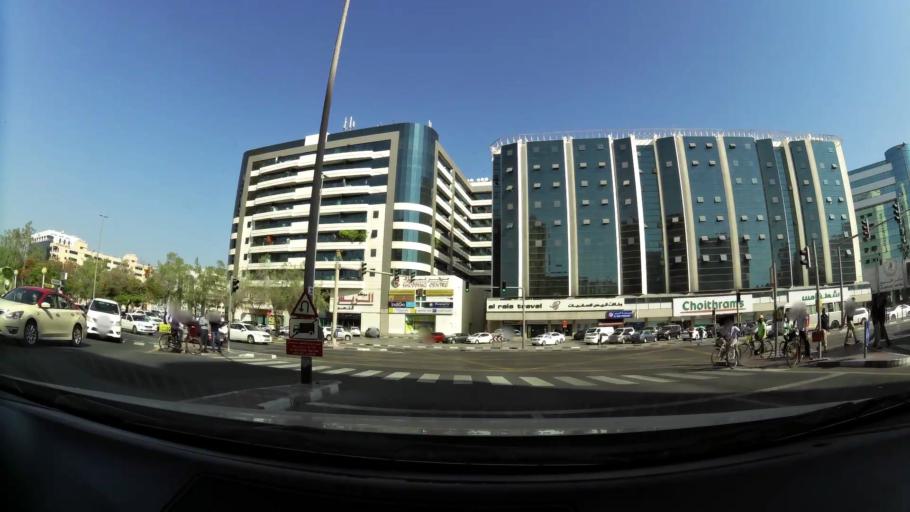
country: AE
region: Ash Shariqah
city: Sharjah
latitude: 25.2557
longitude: 55.2953
